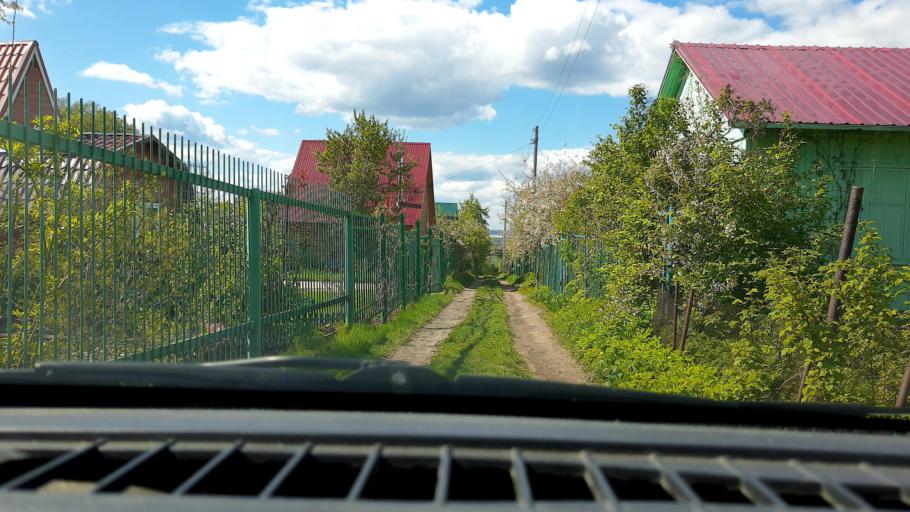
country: RU
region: Nizjnij Novgorod
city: Nizhniy Novgorod
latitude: 56.2182
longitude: 43.9135
